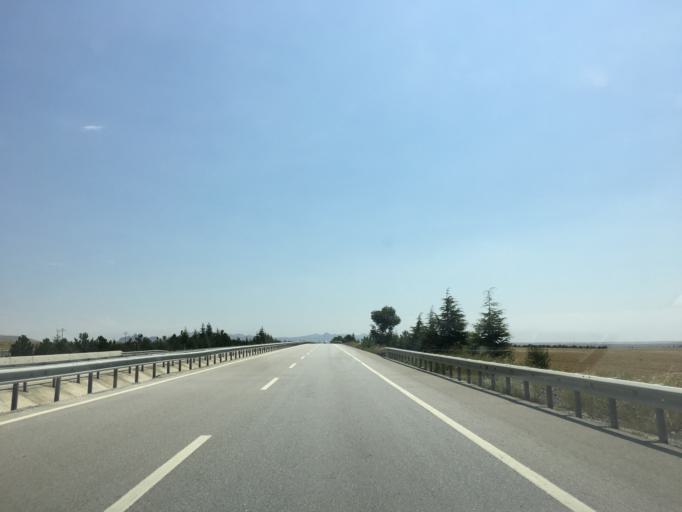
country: TR
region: Eskisehir
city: Sivrihisar
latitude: 39.4606
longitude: 31.3803
